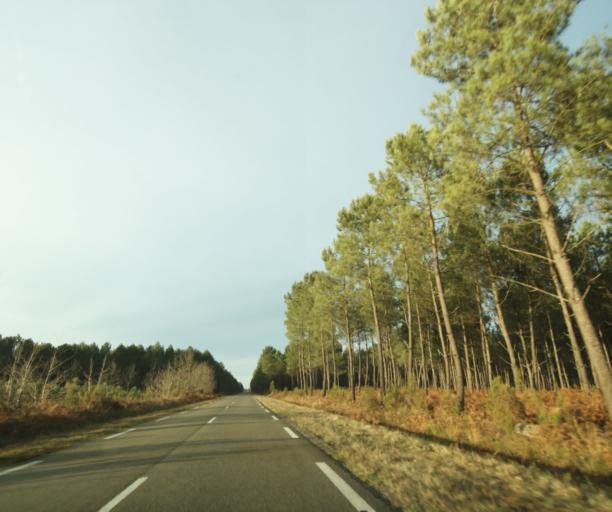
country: FR
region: Aquitaine
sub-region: Departement des Landes
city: Gabarret
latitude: 44.1359
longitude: -0.1175
